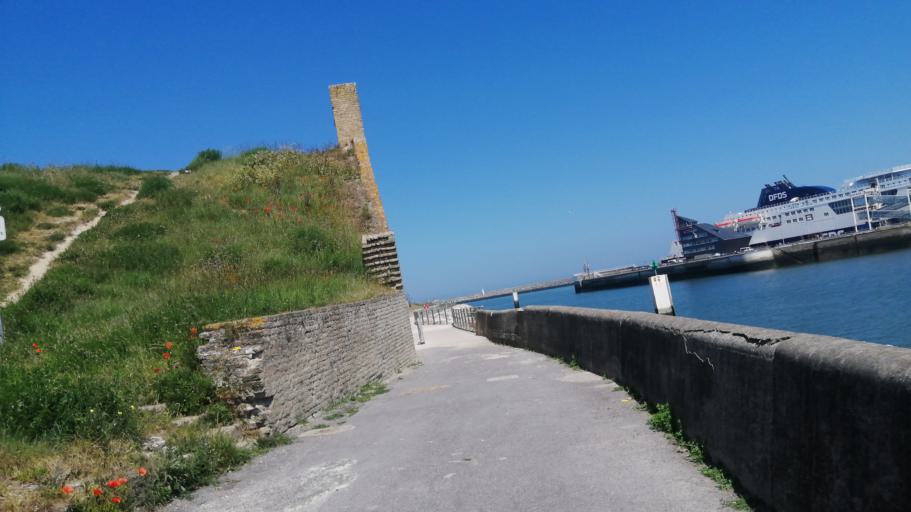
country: FR
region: Nord-Pas-de-Calais
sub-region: Departement du Pas-de-Calais
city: Calais
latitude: 50.9634
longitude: 1.8485
